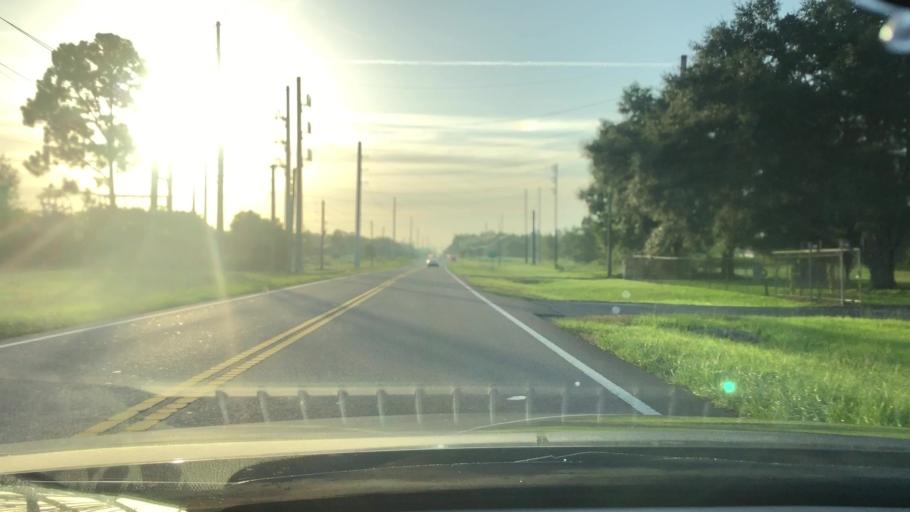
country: US
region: Florida
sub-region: Marion County
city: Belleview
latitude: 29.0261
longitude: -82.2032
